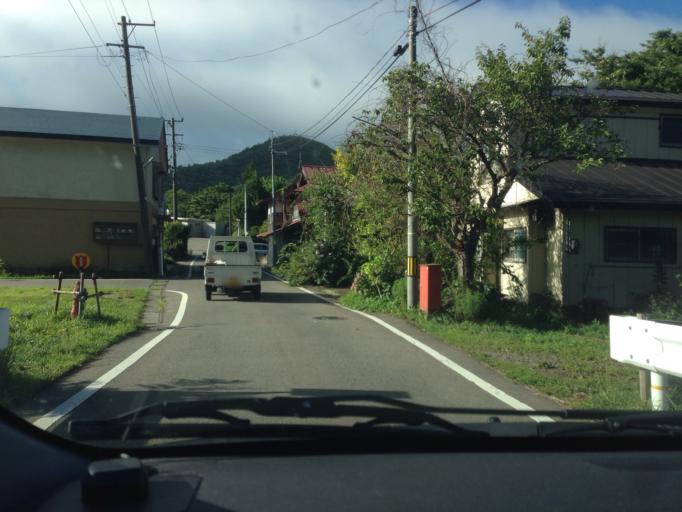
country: JP
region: Fukushima
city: Inawashiro
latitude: 37.4892
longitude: 140.1626
